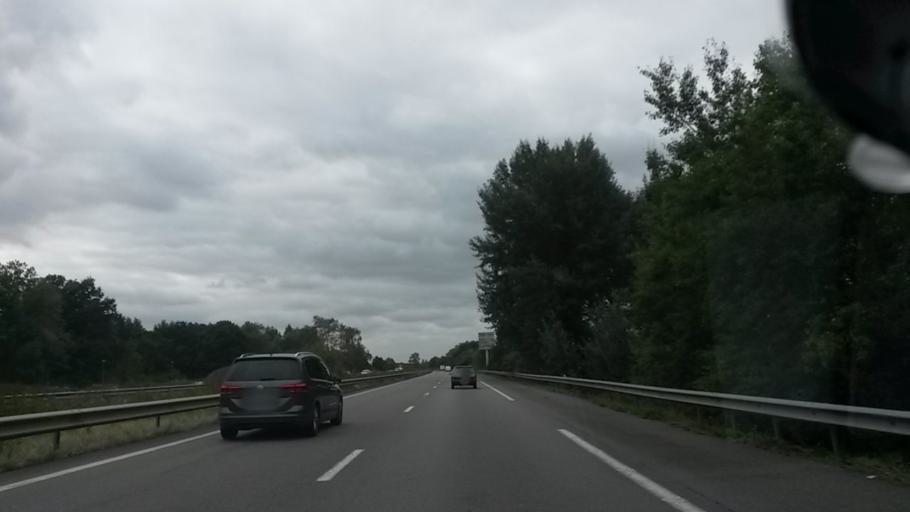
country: FR
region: Nord-Pas-de-Calais
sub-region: Departement du Nord
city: Vicq
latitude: 50.4180
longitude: 3.6308
